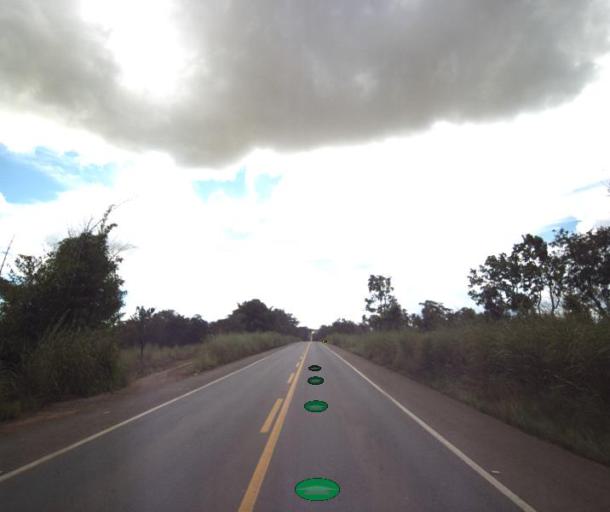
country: BR
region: Goias
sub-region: Jaragua
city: Jaragua
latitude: -15.8763
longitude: -49.2496
